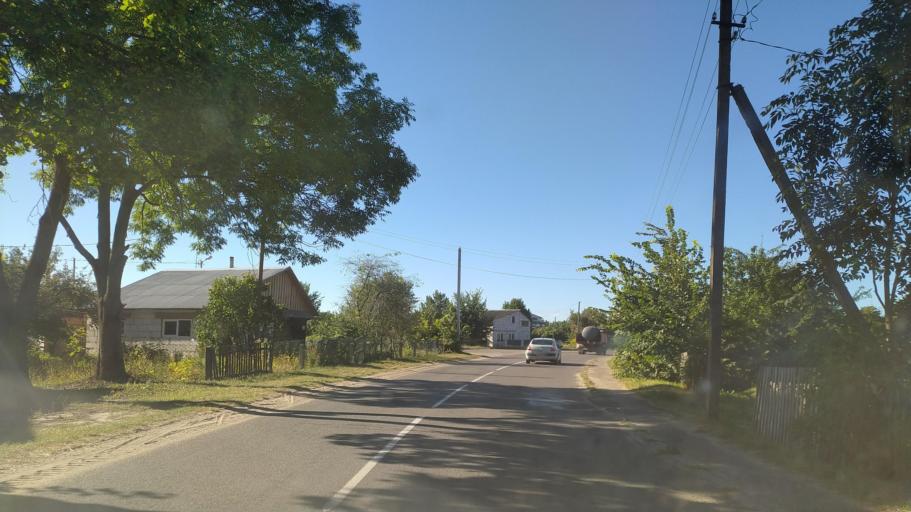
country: BY
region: Brest
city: Pruzhany
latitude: 52.4853
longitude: 24.7074
